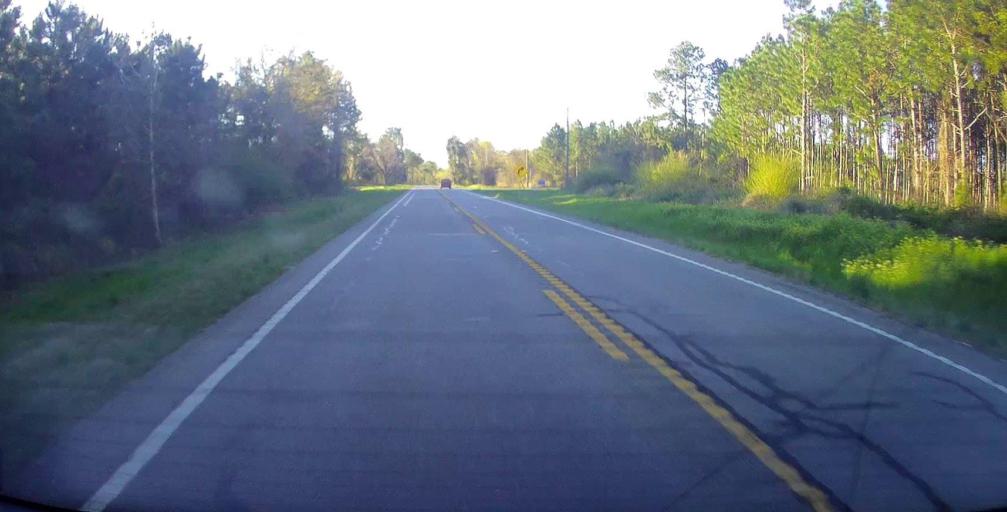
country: US
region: Georgia
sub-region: Wilcox County
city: Abbeville
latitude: 32.0380
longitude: -83.2554
